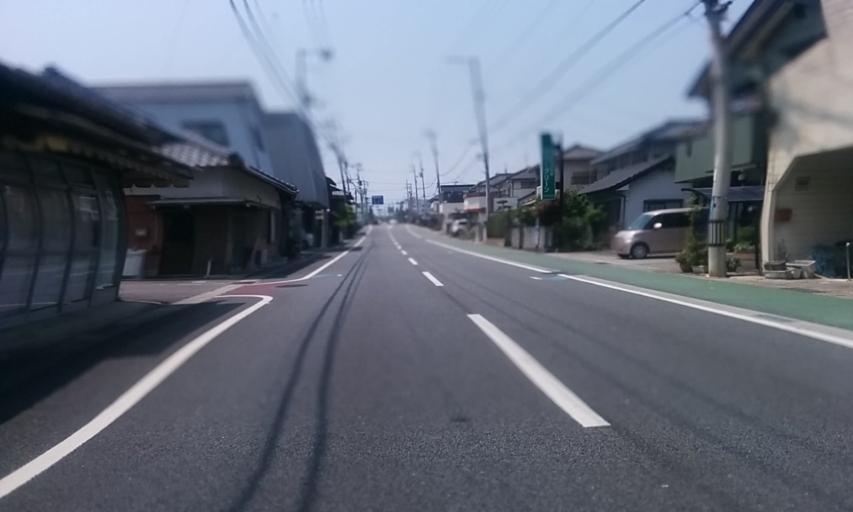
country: JP
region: Ehime
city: Niihama
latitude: 33.9232
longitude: 133.3039
